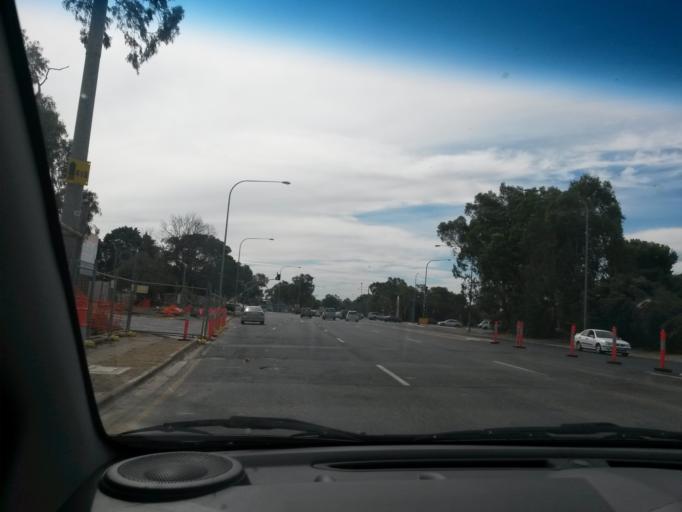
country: AU
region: South Australia
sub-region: Salisbury
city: Salisbury
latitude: -34.7668
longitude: 138.6706
